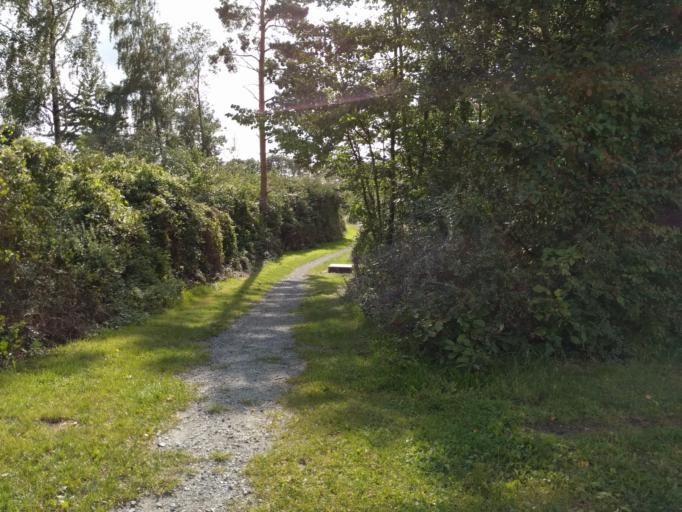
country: DK
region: South Denmark
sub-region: Kerteminde Kommune
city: Munkebo
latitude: 55.4553
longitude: 10.5440
